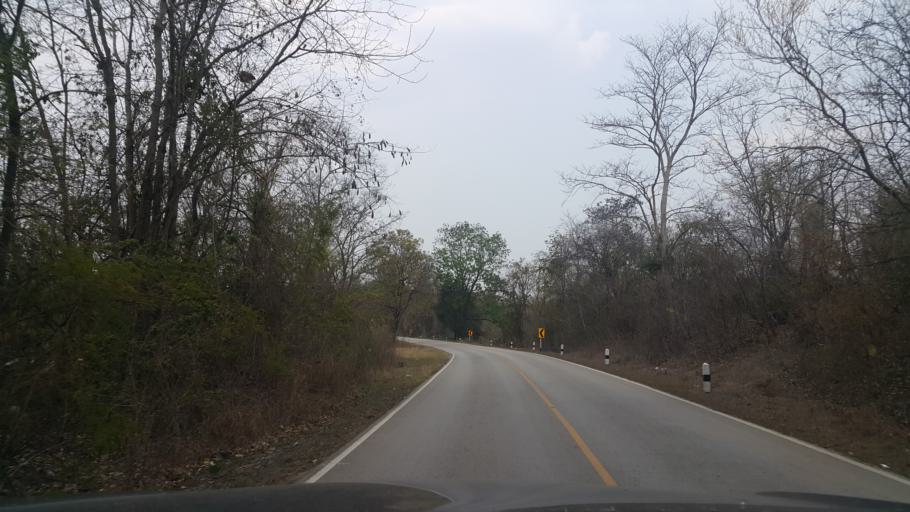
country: TH
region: Lampang
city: Soem Ngam
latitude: 17.9881
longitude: 99.1676
